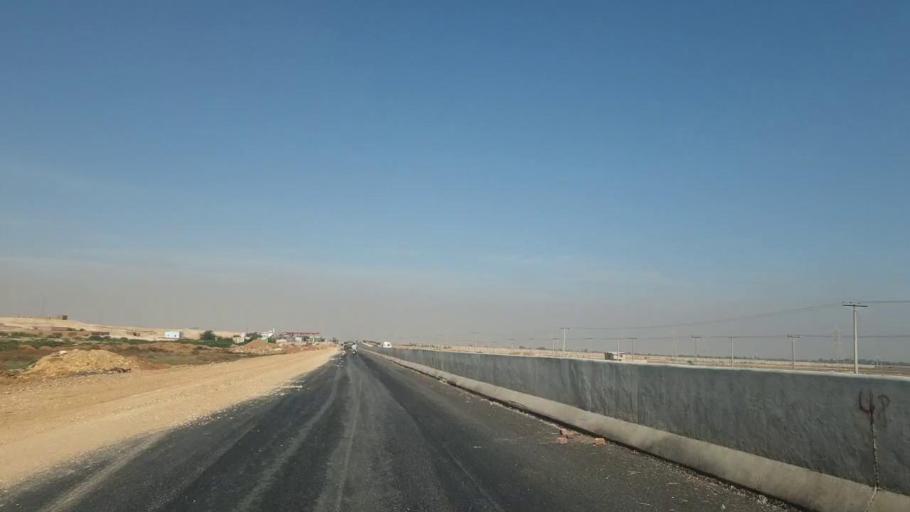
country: PK
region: Sindh
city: Jamshoro
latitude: 25.4951
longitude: 68.2722
